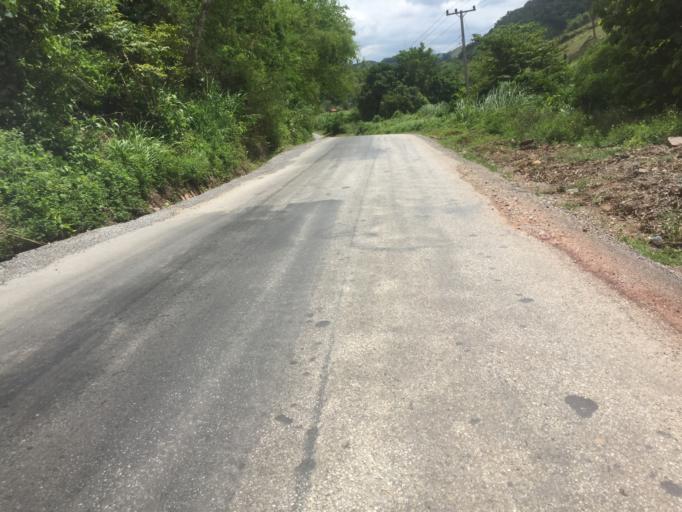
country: LA
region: Oudomxai
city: Muang Xay
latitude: 20.7431
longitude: 102.0294
